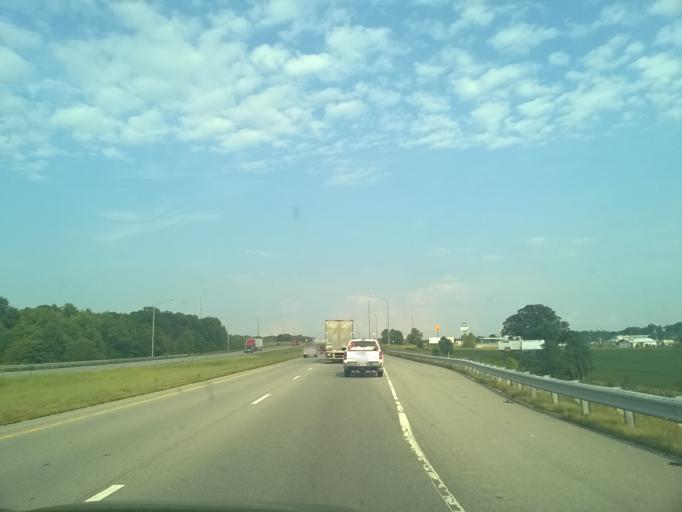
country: US
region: Indiana
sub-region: Putnam County
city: Cloverdale
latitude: 39.5327
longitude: -86.8105
